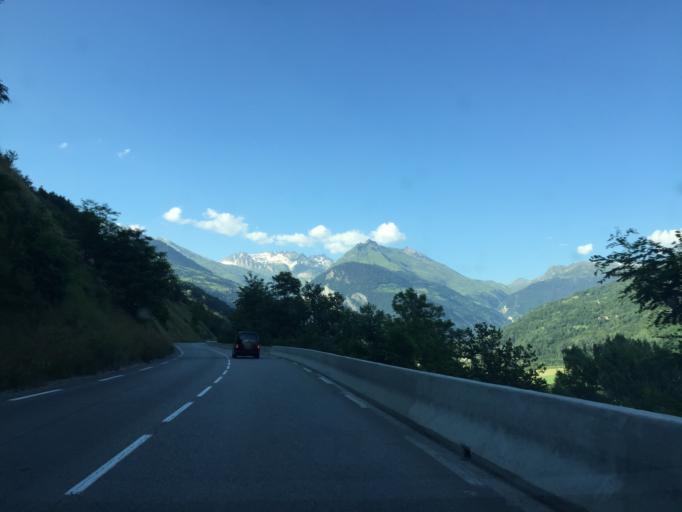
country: FR
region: Rhone-Alpes
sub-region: Departement de la Savoie
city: Bourg-Saint-Maurice
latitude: 45.5919
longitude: 6.7479
